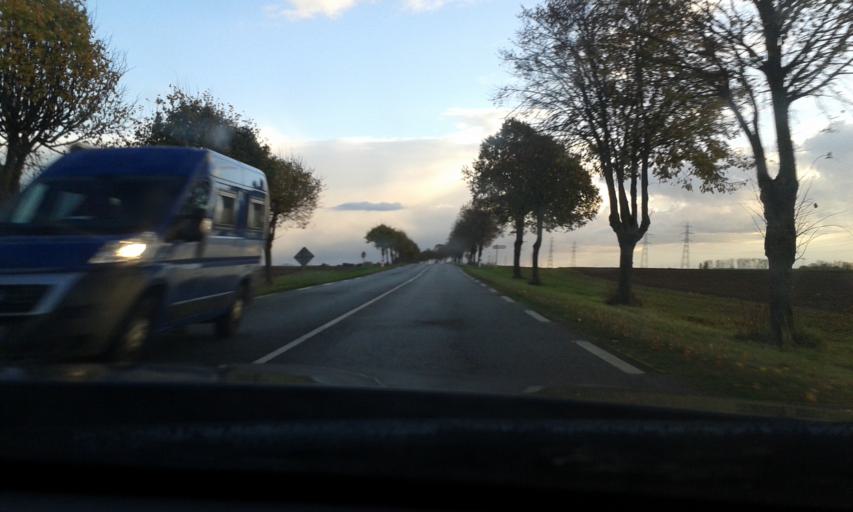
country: FR
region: Centre
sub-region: Departement d'Eure-et-Loir
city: Baigneaux
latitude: 48.1528
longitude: 1.8439
